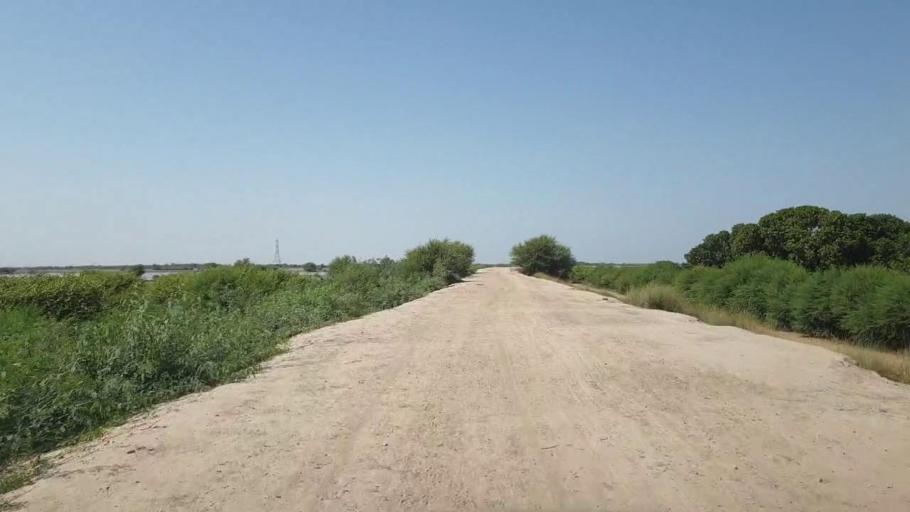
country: PK
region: Sindh
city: Matiari
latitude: 25.6356
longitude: 68.4875
